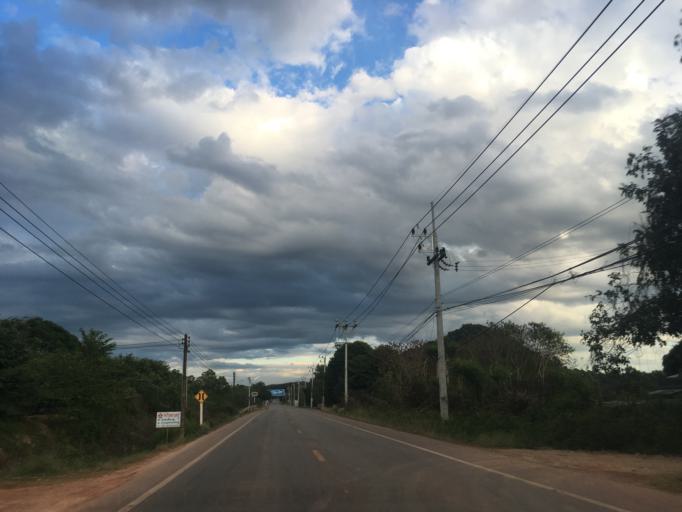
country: TH
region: Chanthaburi
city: Na Yai Am
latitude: 12.6838
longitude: 101.8363
